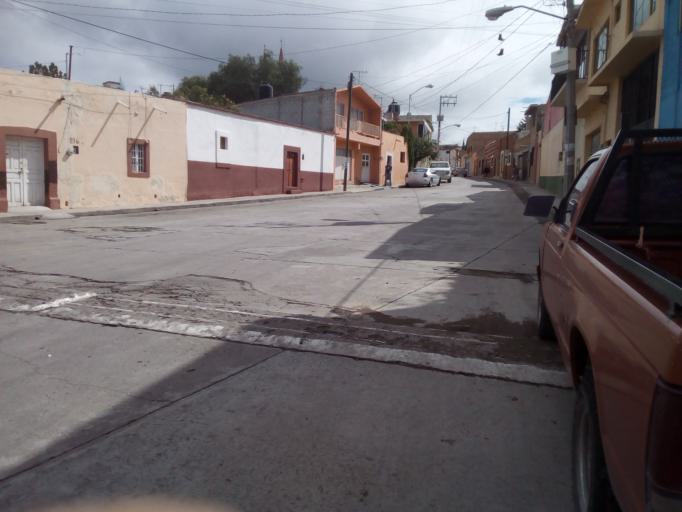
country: MX
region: Guerrero
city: San Luis de la Paz
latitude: 21.2964
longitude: -100.5129
